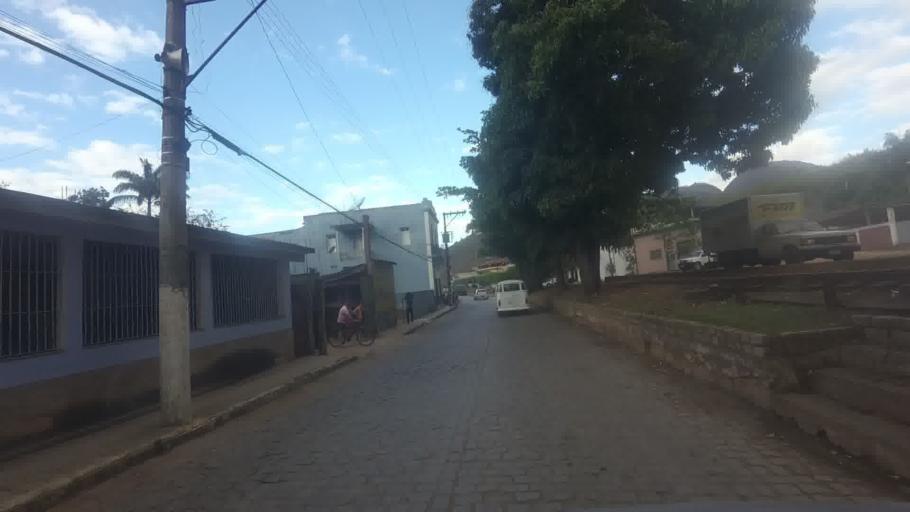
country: BR
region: Espirito Santo
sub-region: Mimoso Do Sul
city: Mimoso do Sul
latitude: -20.9548
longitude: -41.3515
